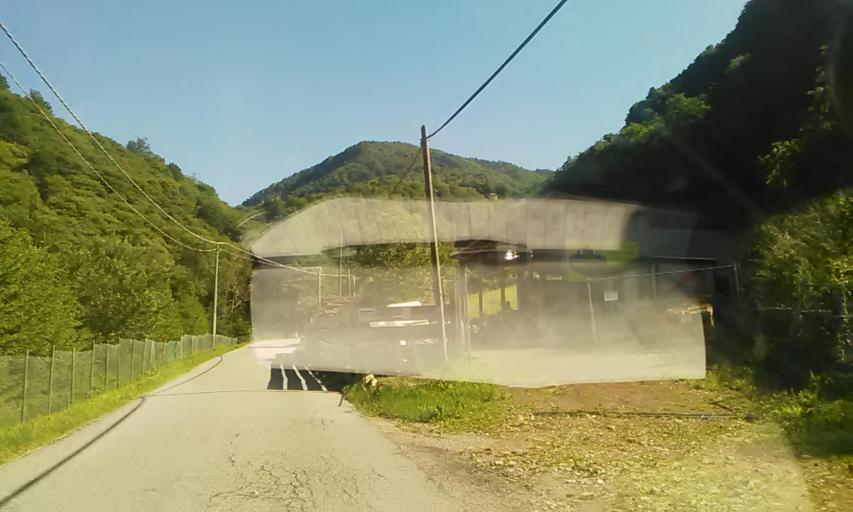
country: IT
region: Piedmont
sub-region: Provincia di Vercelli
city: Varallo
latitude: 45.8213
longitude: 8.2760
